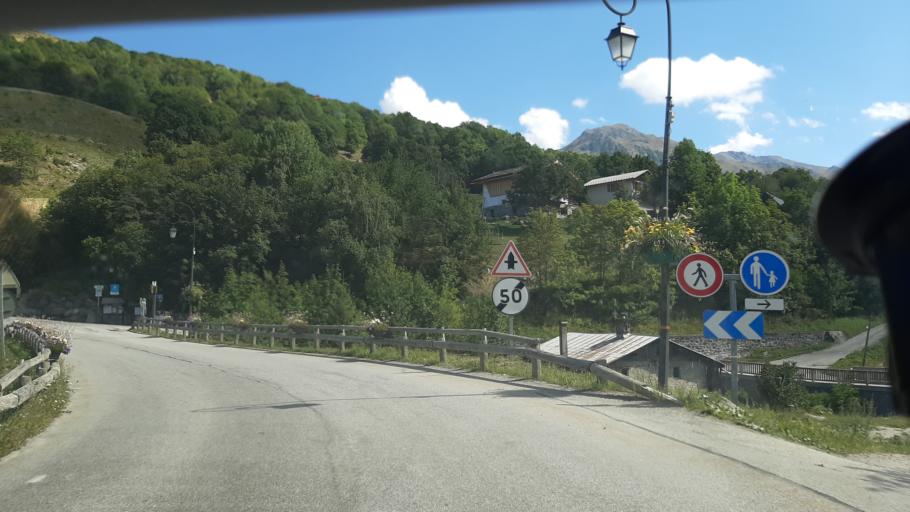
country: FR
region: Rhone-Alpes
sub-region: Departement de la Savoie
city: Saint-Michel-de-Maurienne
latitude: 45.1816
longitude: 6.4795
